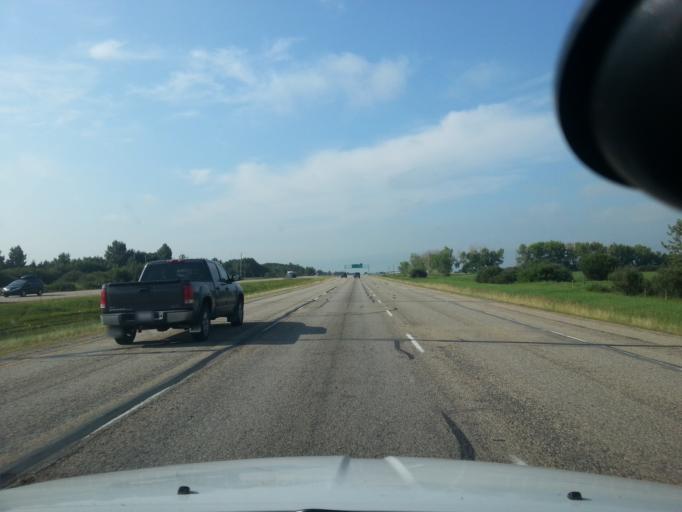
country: CA
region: Alberta
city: Lacombe
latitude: 52.5242
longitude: -113.6773
